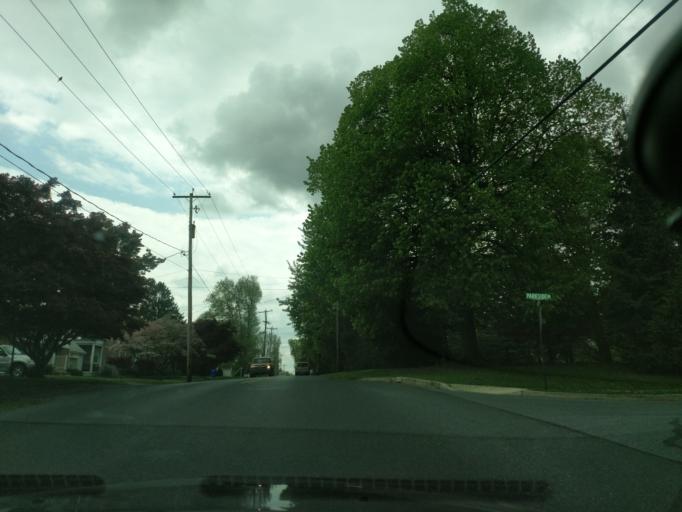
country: US
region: Pennsylvania
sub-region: Lebanon County
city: Lebanon South
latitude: 40.3275
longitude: -76.4110
